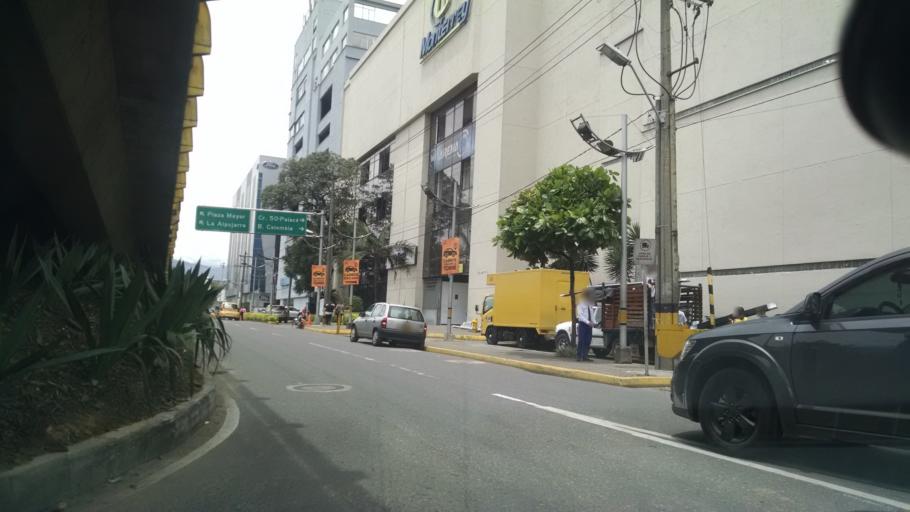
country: CO
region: Antioquia
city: Itagui
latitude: 6.2142
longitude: -75.5774
